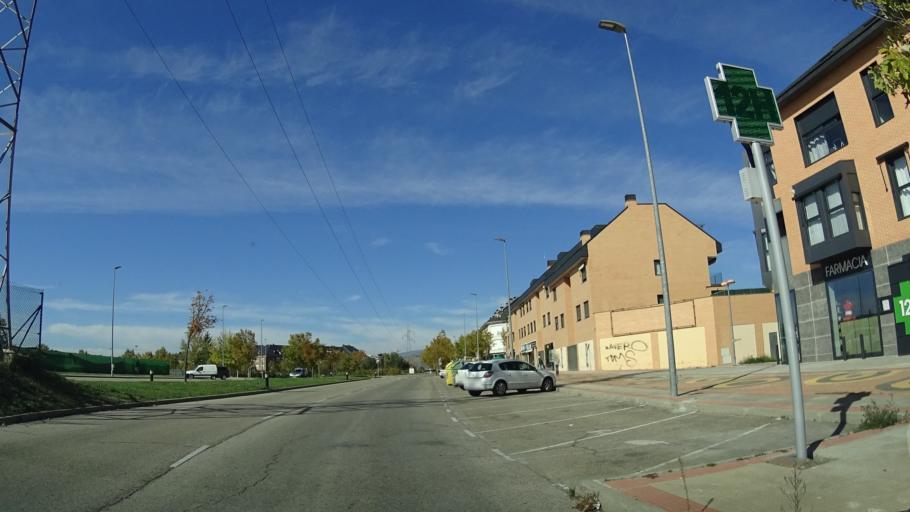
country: ES
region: Madrid
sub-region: Provincia de Madrid
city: Villanueva del Pardillo
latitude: 40.4938
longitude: -3.9611
